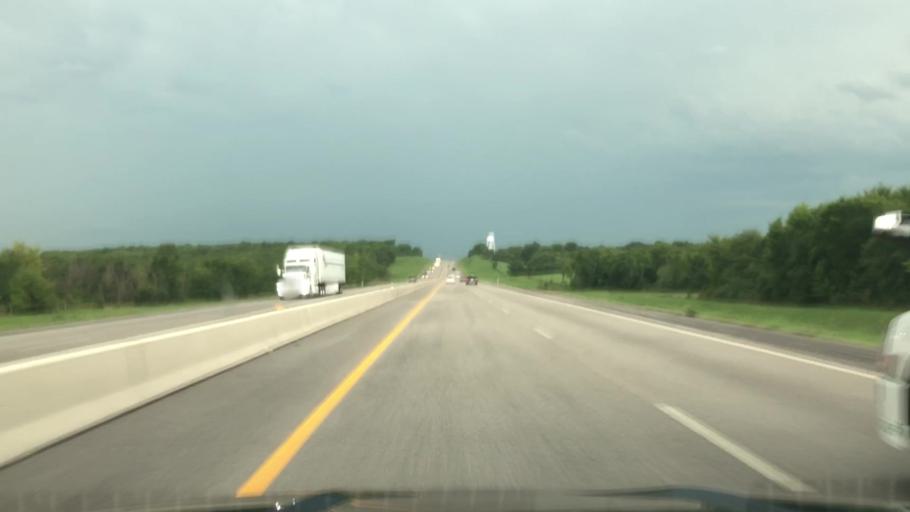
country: US
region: Oklahoma
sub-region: Rogers County
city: Justice
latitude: 36.3271
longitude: -95.5327
